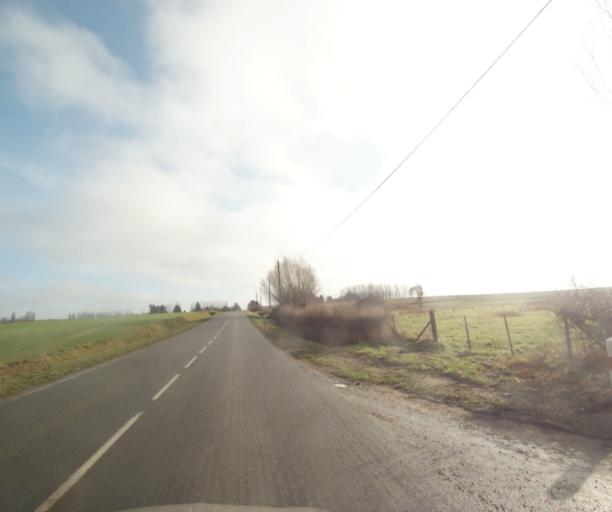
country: FR
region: Nord-Pas-de-Calais
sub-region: Departement du Nord
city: Saulzoir
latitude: 50.2718
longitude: 3.4564
